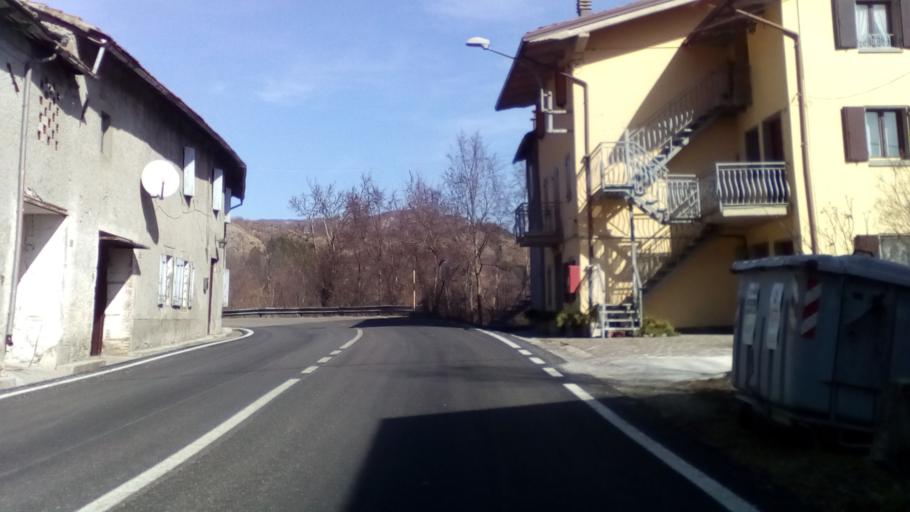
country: IT
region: Emilia-Romagna
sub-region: Provincia di Modena
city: Riolunato
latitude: 44.2330
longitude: 10.6253
